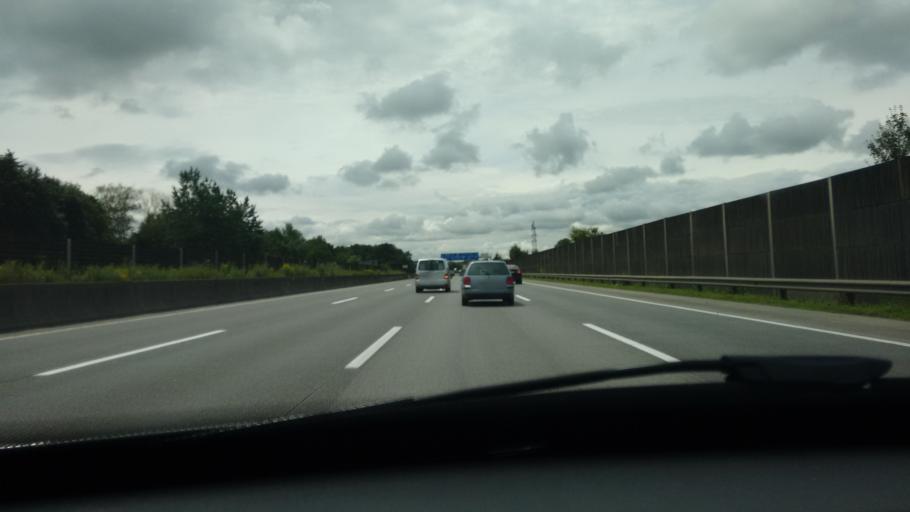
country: AT
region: Upper Austria
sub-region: Politischer Bezirk Linz-Land
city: Traun
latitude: 48.1994
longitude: 14.2483
